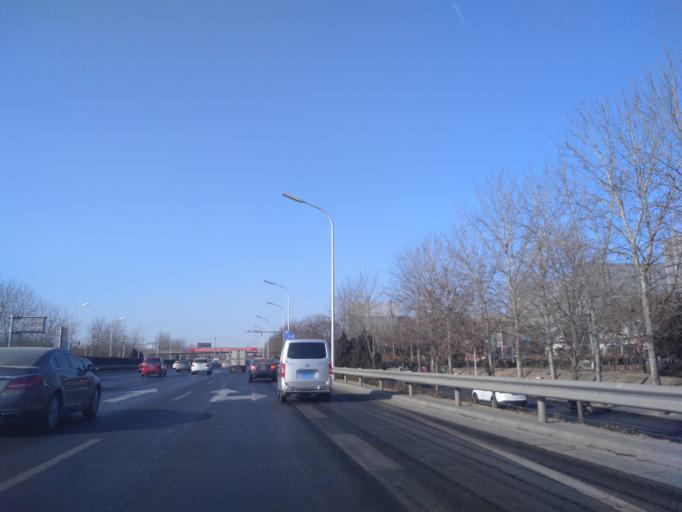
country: CN
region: Beijing
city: Jiugong
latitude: 39.8320
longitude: 116.4506
